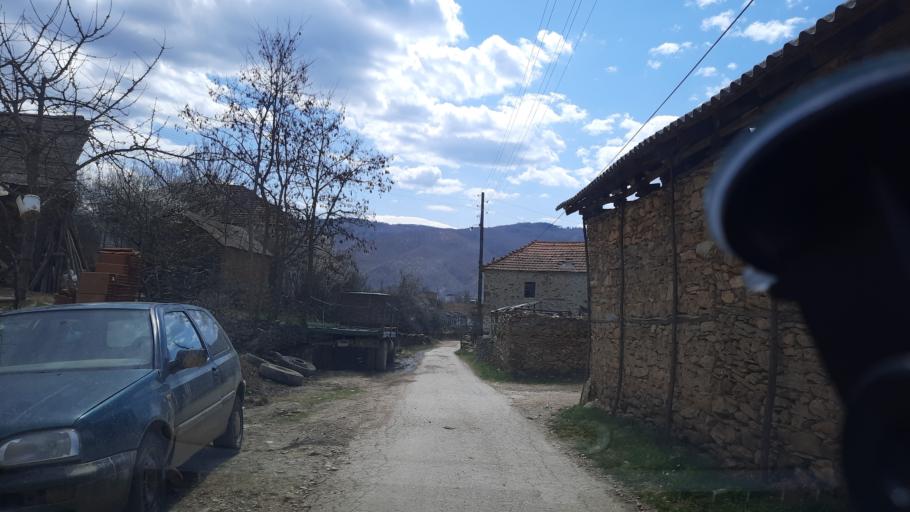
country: MK
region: Demir Hisar
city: Sopotnica
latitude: 41.3010
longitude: 21.1527
